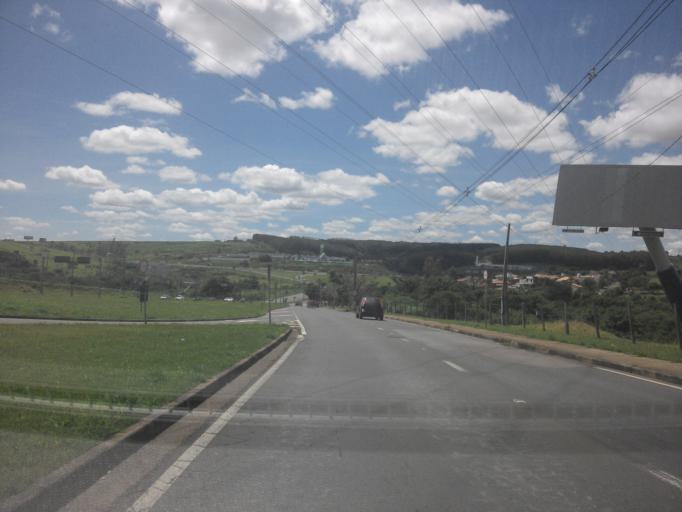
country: BR
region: Sao Paulo
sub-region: Campinas
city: Campinas
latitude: -22.8897
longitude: -47.0186
